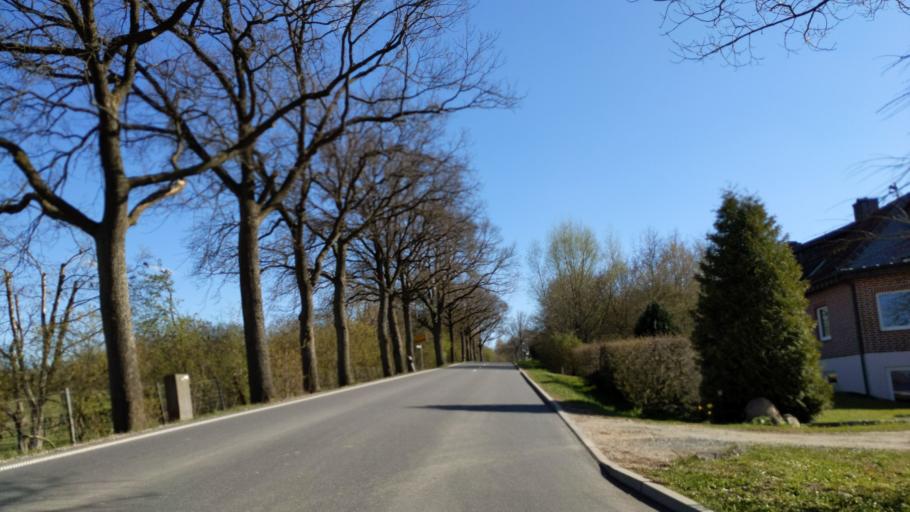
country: DE
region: Schleswig-Holstein
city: Eutin
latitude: 54.0889
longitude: 10.6190
